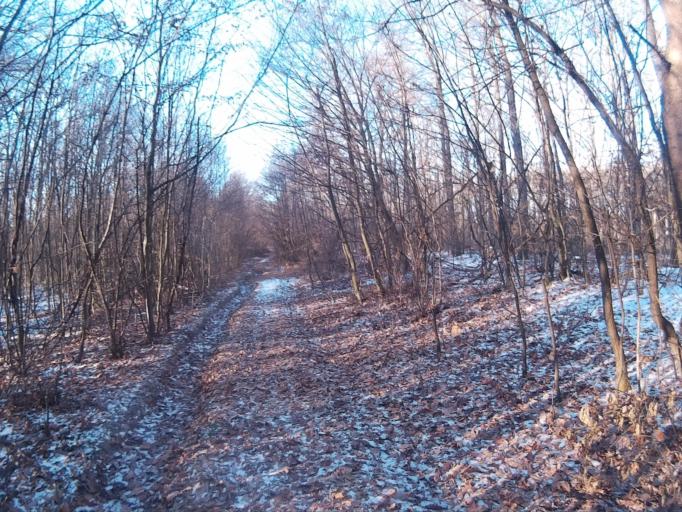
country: HU
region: Borsod-Abauj-Zemplen
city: Putnok
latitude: 48.4625
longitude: 20.4659
